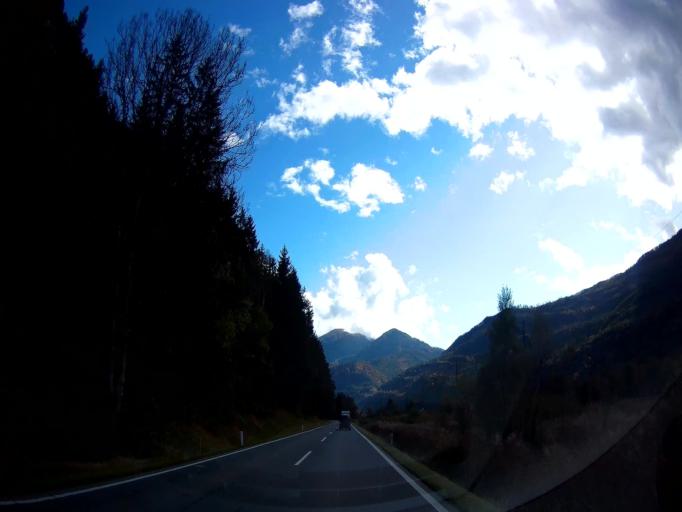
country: AT
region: Carinthia
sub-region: Politischer Bezirk Spittal an der Drau
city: Oberdrauburg
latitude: 46.7604
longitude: 12.9395
